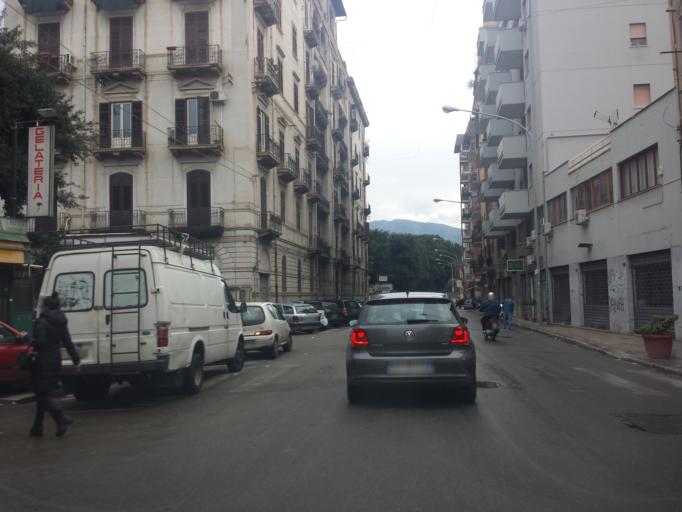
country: IT
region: Sicily
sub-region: Palermo
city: Palermo
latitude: 38.1157
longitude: 13.3513
